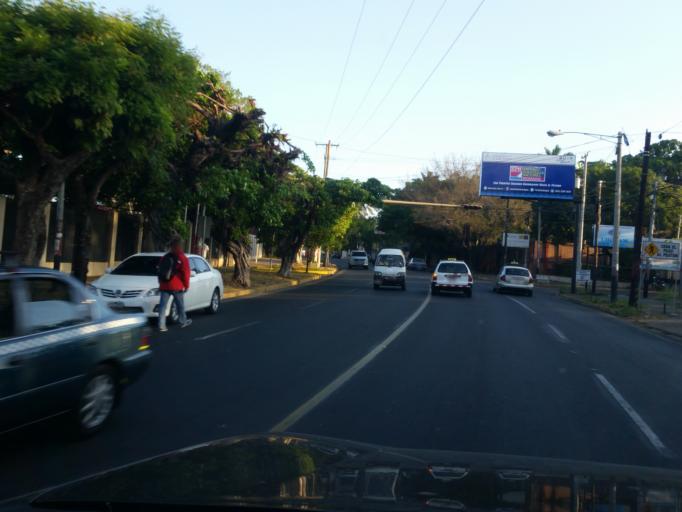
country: NI
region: Managua
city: Managua
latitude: 12.1386
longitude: -86.2829
